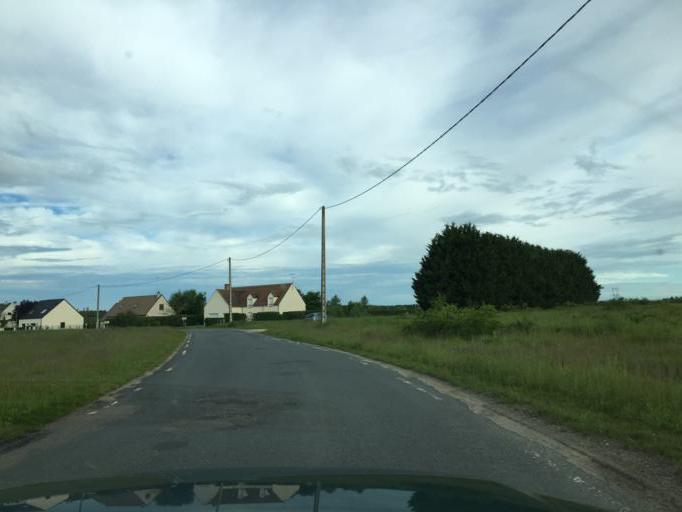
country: FR
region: Centre
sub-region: Departement du Loiret
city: Ingre
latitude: 47.9022
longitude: 1.8091
